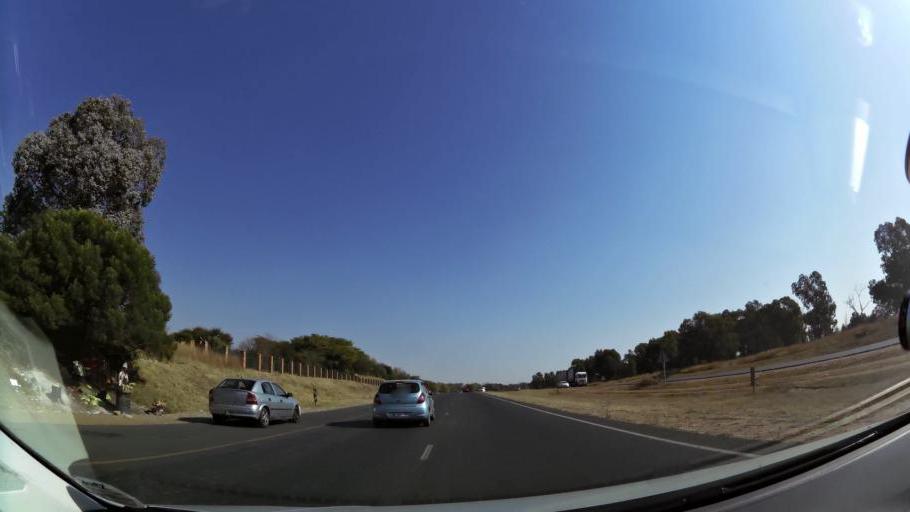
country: ZA
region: Gauteng
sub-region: City of Johannesburg Metropolitan Municipality
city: Modderfontein
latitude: -26.1081
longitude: 28.1660
